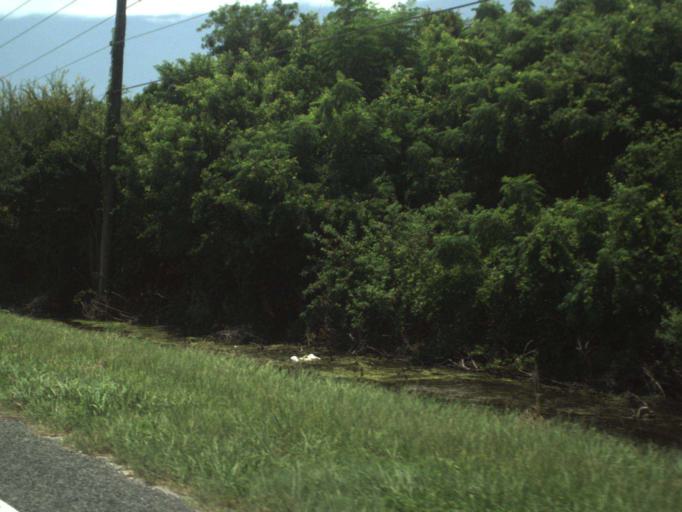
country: US
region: Florida
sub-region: Indian River County
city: Sebastian
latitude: 27.8024
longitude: -80.4630
